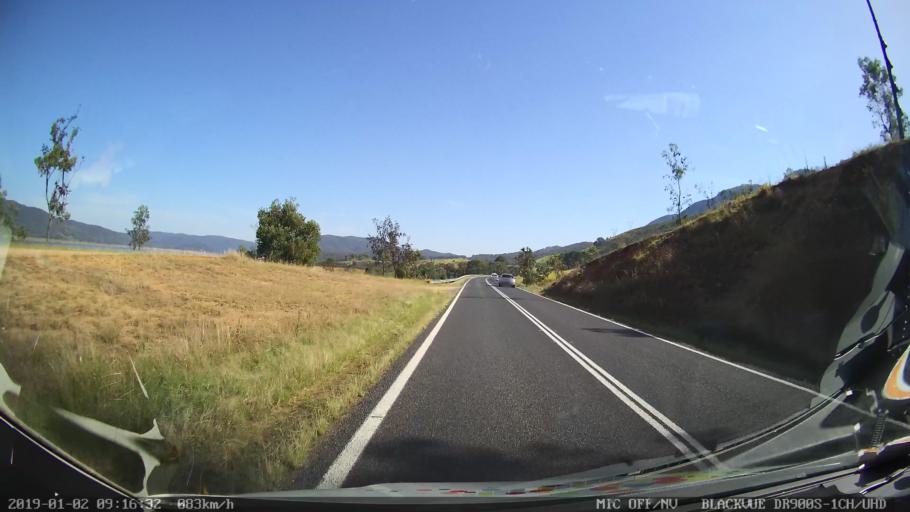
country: AU
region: New South Wales
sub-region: Tumut Shire
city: Tumut
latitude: -35.4523
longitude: 148.2843
